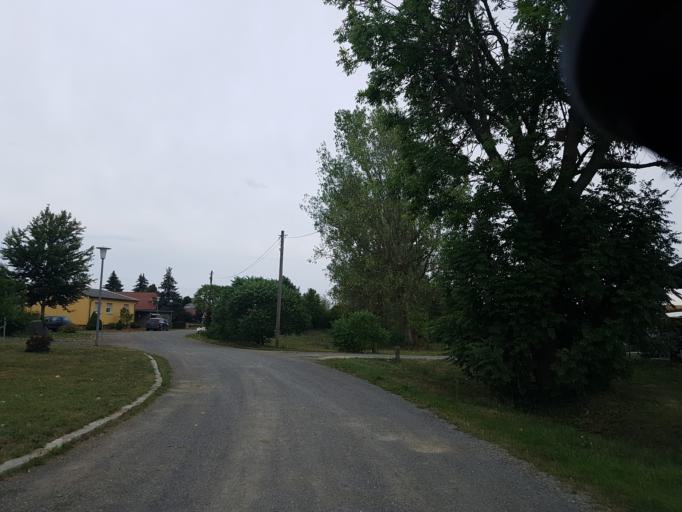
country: DE
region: Brandenburg
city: Finsterwalde
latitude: 51.6095
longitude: 13.6435
